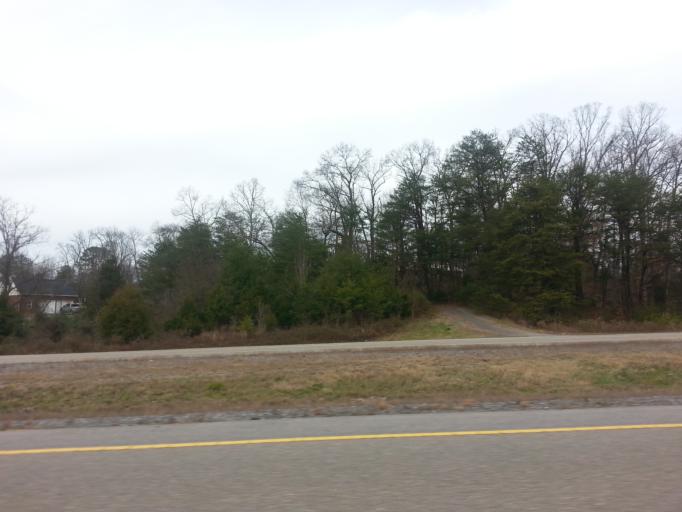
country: US
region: Tennessee
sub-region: Cocke County
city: Newport
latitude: 35.9925
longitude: -83.1149
